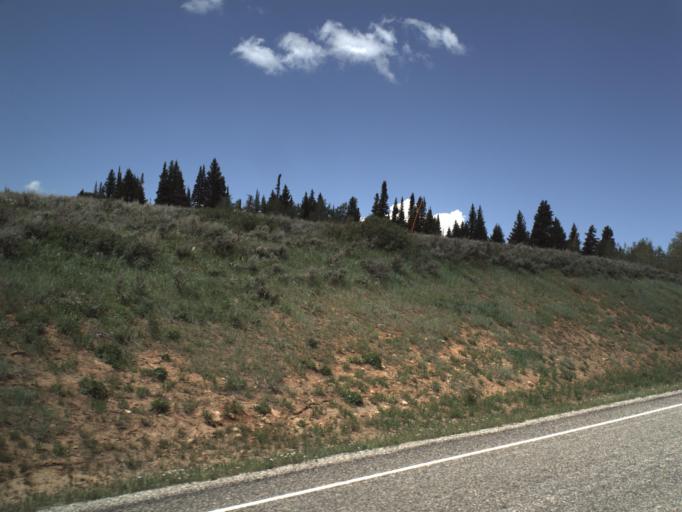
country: US
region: Utah
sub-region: Weber County
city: Wolf Creek
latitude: 41.4422
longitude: -111.5063
